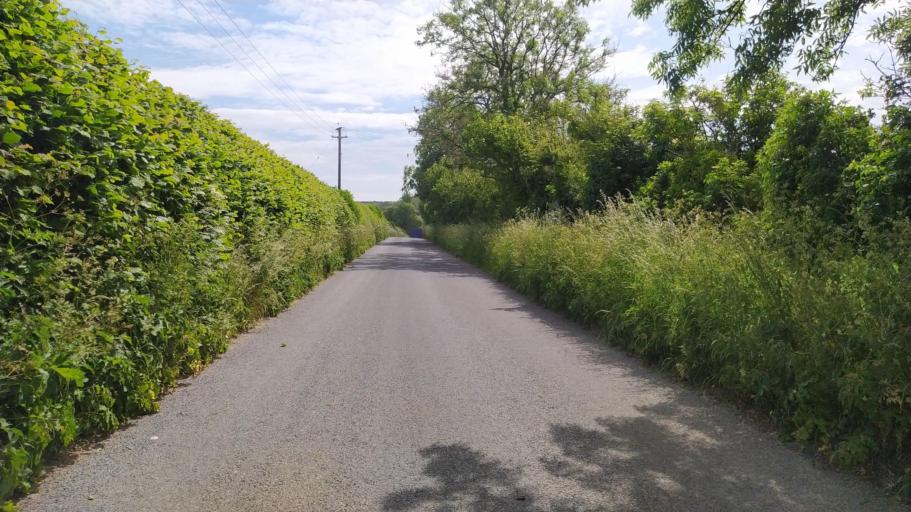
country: GB
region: England
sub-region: Dorset
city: Dorchester
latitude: 50.8006
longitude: -2.5234
